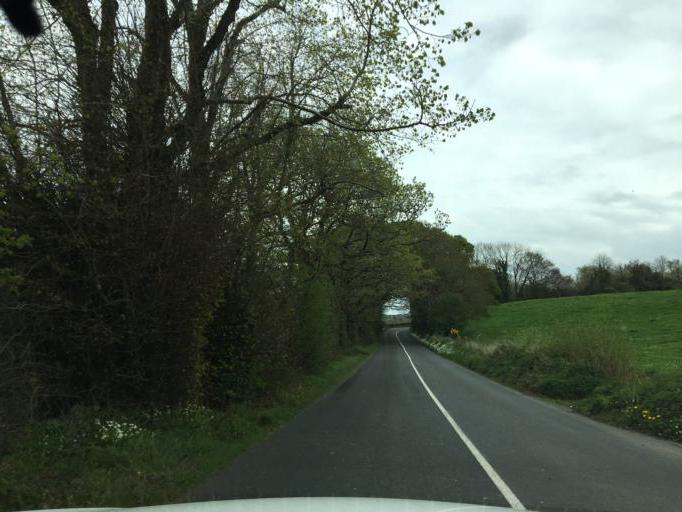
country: IE
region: Leinster
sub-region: Loch Garman
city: Loch Garman
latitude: 52.3578
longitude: -6.5485
